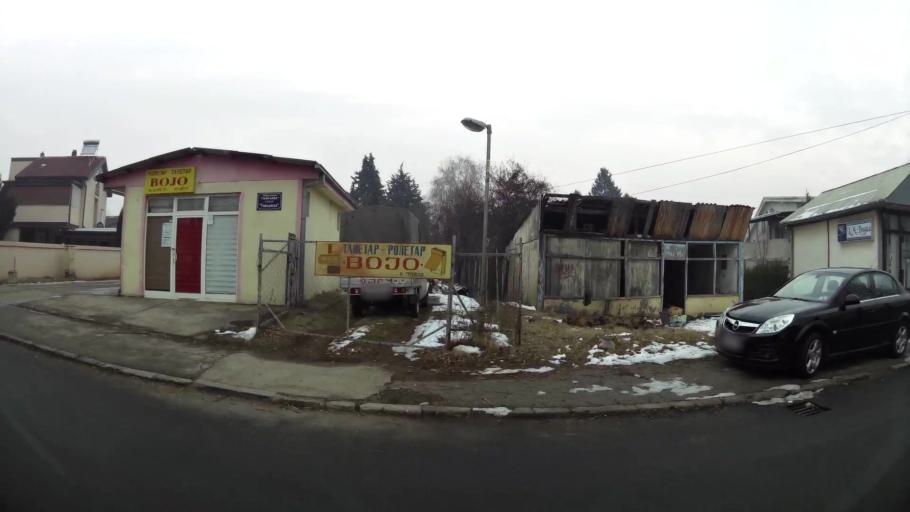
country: MK
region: Cair
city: Cair
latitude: 42.0140
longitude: 21.4604
